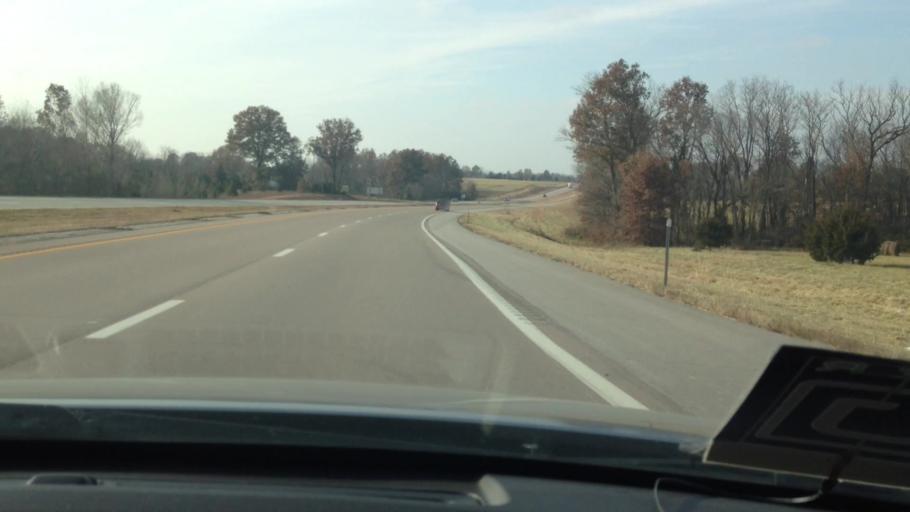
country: US
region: Missouri
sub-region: Cass County
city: Garden City
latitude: 38.4688
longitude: -94.0090
